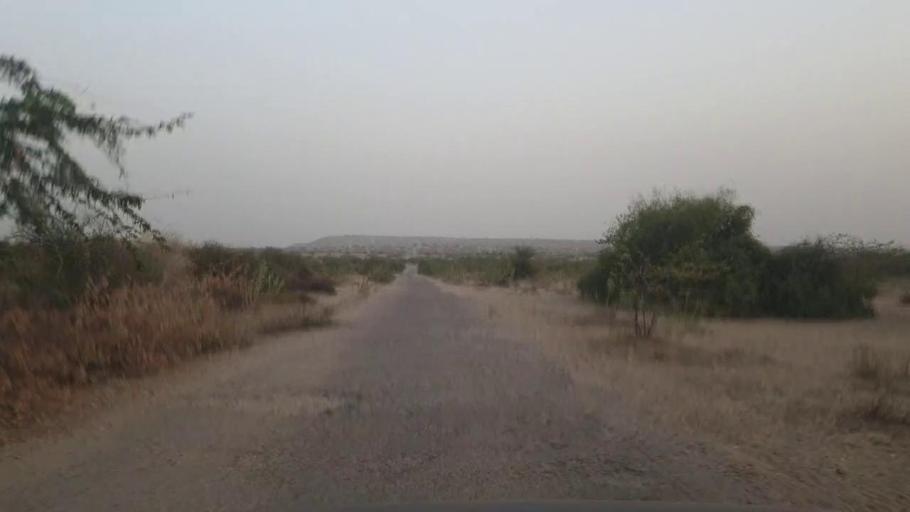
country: PK
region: Sindh
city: Chor
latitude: 25.5106
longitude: 69.8160
